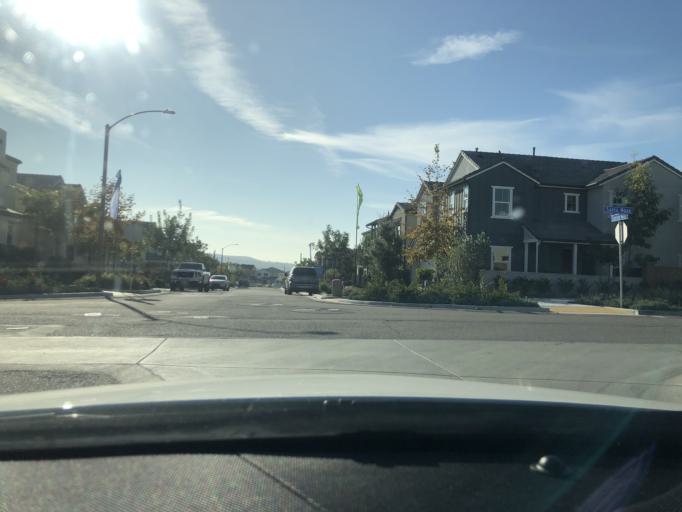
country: US
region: California
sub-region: San Diego County
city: Bonita
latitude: 32.5971
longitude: -117.0032
